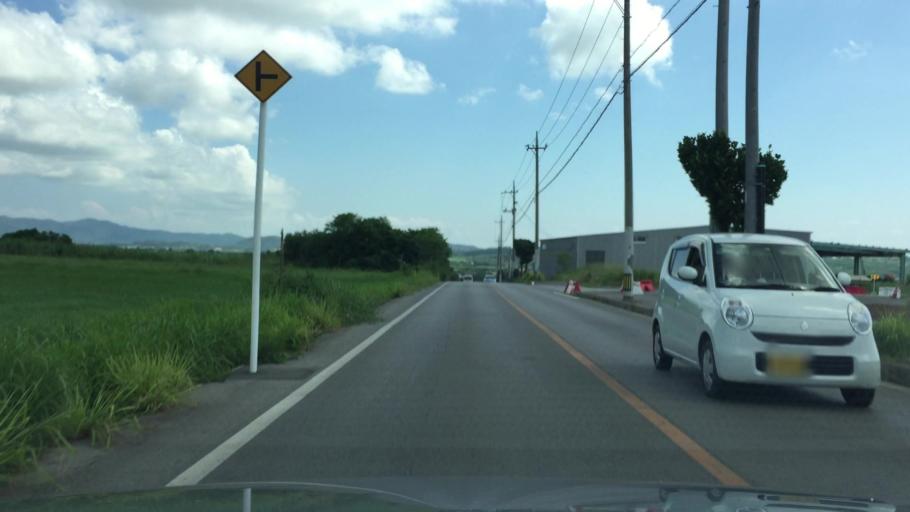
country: JP
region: Okinawa
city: Ishigaki
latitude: 24.3523
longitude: 124.1892
